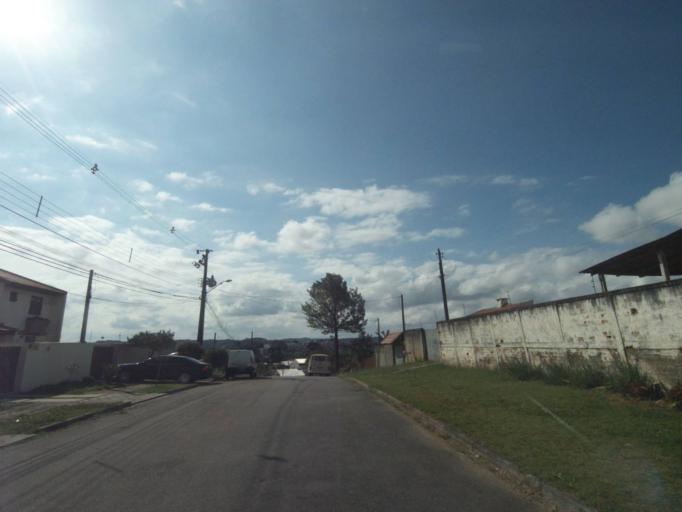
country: BR
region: Parana
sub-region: Curitiba
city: Curitiba
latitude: -25.3832
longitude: -49.2954
